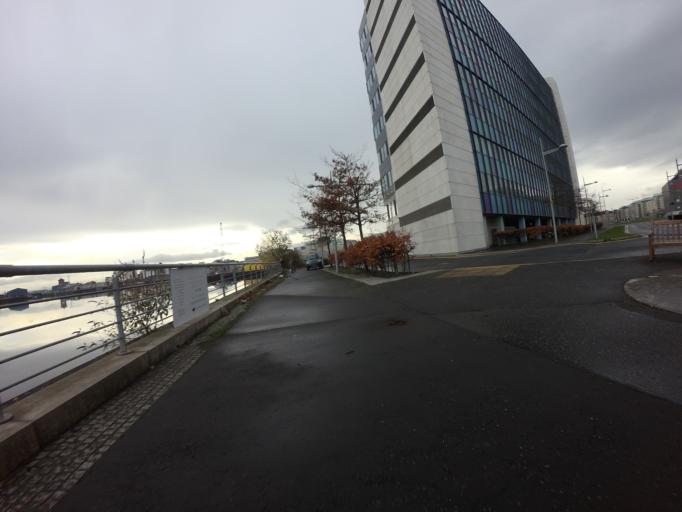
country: GB
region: Scotland
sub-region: West Lothian
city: Seafield
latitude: 55.9818
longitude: -3.1745
